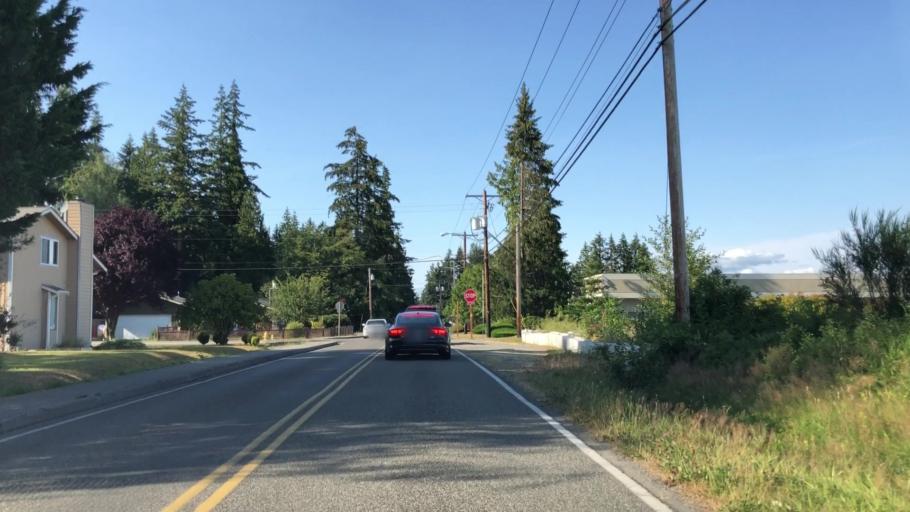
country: US
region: Washington
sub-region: Snohomish County
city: Mukilteo
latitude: 47.9251
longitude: -122.2932
